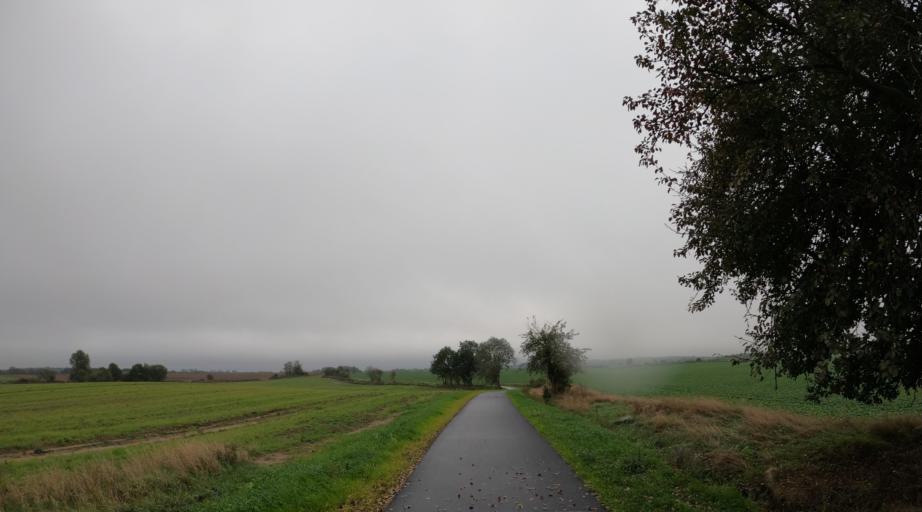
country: PL
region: West Pomeranian Voivodeship
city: Trzcinsko Zdroj
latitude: 52.9275
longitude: 14.7298
